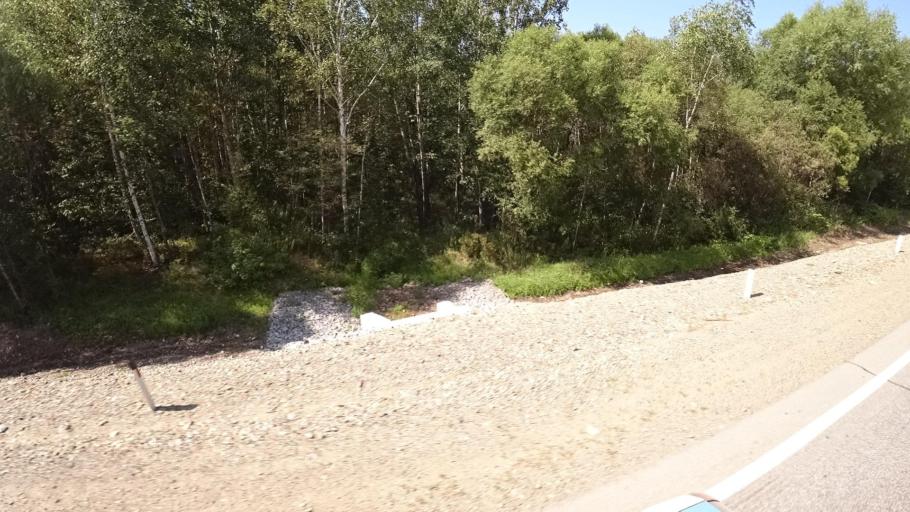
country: RU
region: Khabarovsk Krai
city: Khor
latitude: 47.9829
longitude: 135.0878
